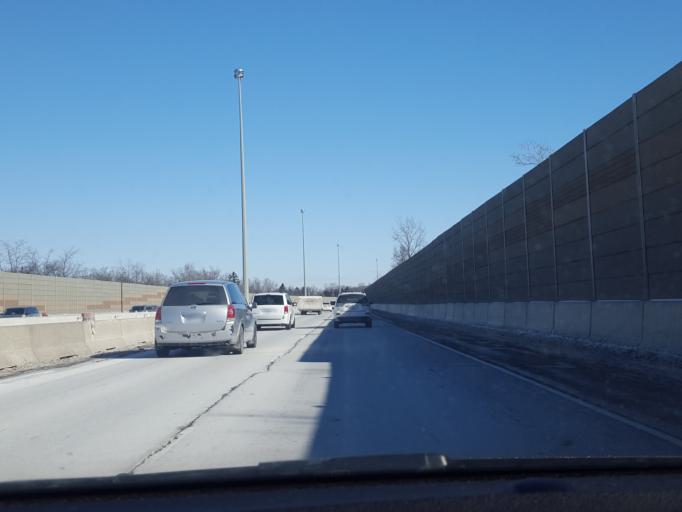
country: CA
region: Ontario
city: Kitchener
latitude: 43.4241
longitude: -80.4990
